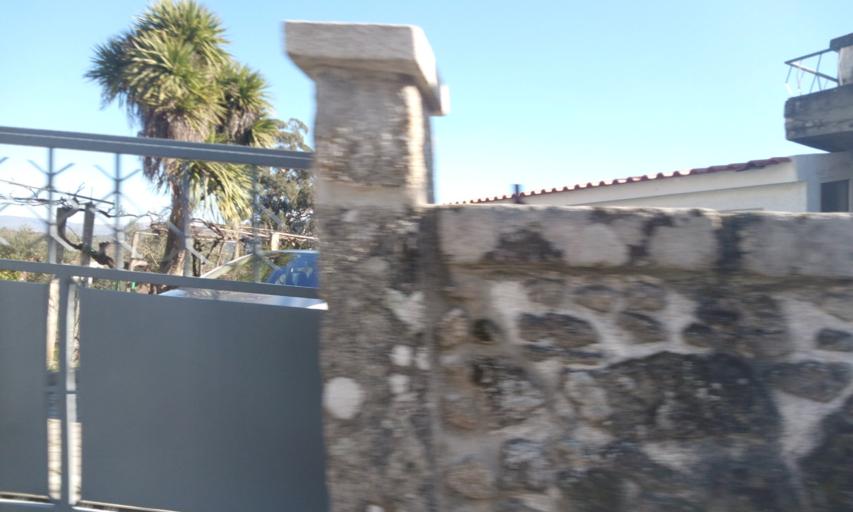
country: PT
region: Guarda
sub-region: Manteigas
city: Manteigas
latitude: 40.5134
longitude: -7.6080
